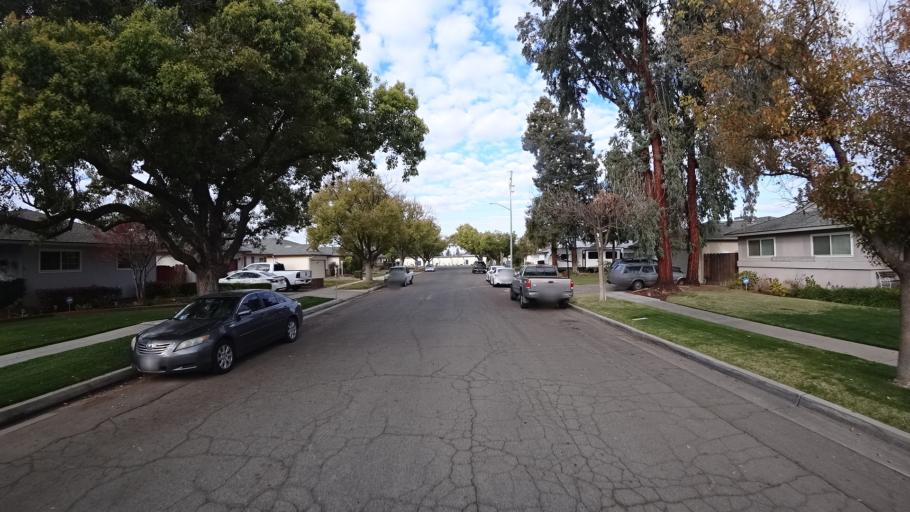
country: US
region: California
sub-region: Fresno County
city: Clovis
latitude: 36.8260
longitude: -119.7664
